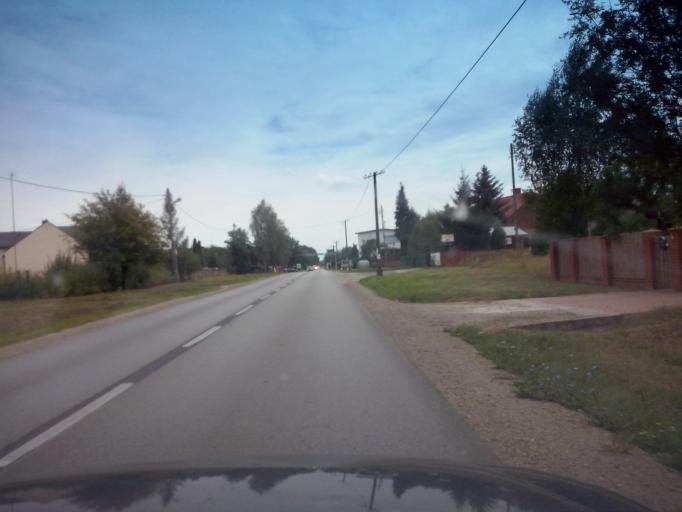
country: PL
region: Subcarpathian Voivodeship
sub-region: Powiat stalowowolski
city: Stalowa Wola
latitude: 50.6041
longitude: 22.0206
